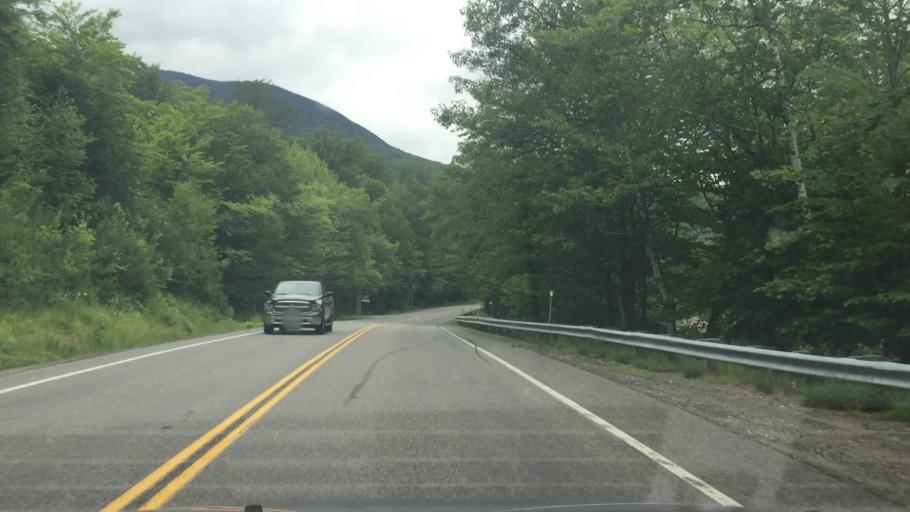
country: US
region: New Hampshire
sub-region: Carroll County
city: North Conway
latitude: 44.0762
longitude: -71.3268
